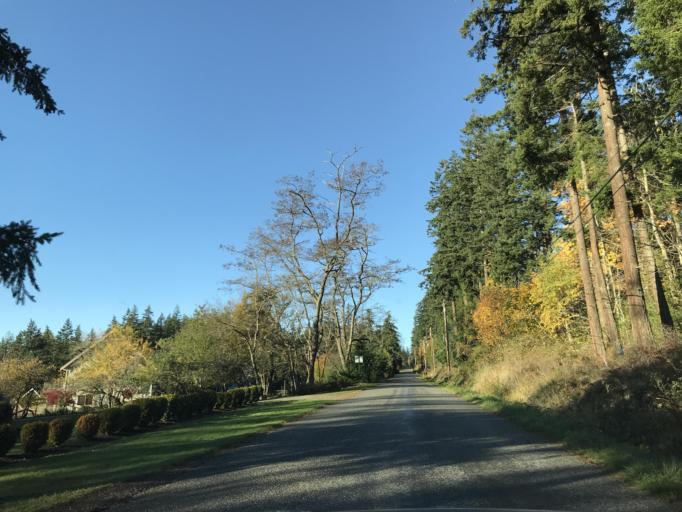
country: US
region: Washington
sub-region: Whatcom County
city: Geneva
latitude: 48.7710
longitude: -122.3991
